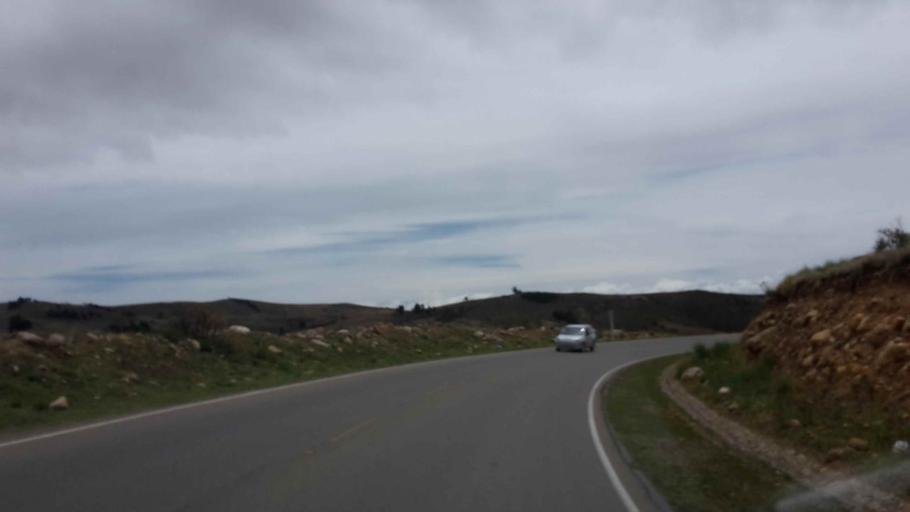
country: BO
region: Cochabamba
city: Arani
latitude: -17.4689
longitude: -65.6601
